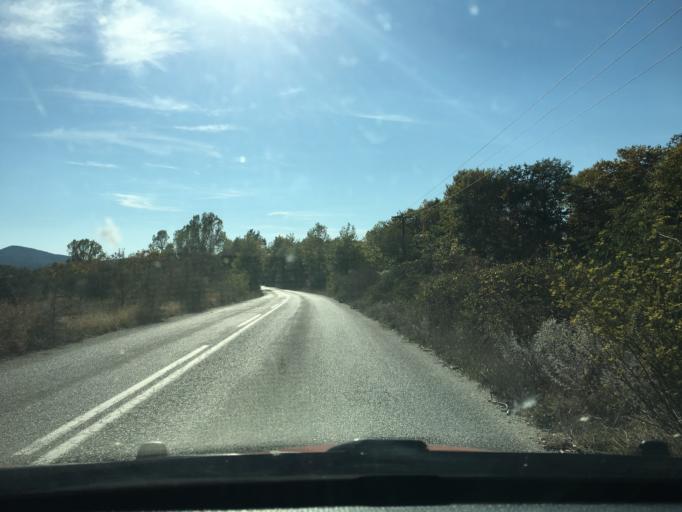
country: GR
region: Central Macedonia
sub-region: Nomos Chalkidikis
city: Megali Panagia
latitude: 40.3817
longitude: 23.7015
